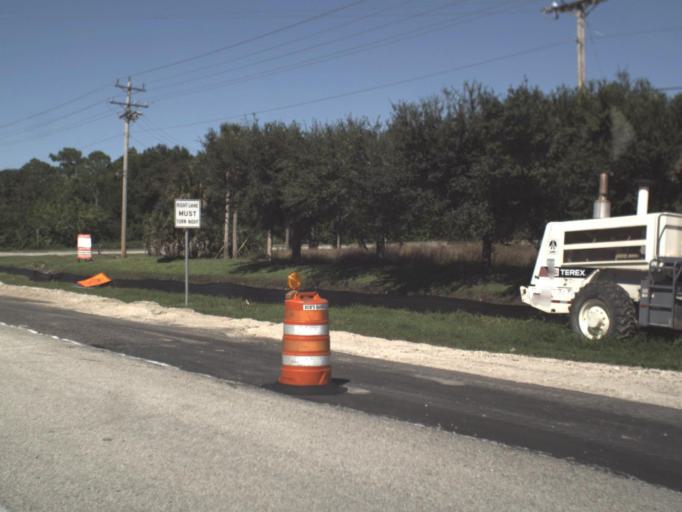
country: US
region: Florida
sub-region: Lee County
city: Suncoast Estates
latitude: 26.7394
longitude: -81.9143
